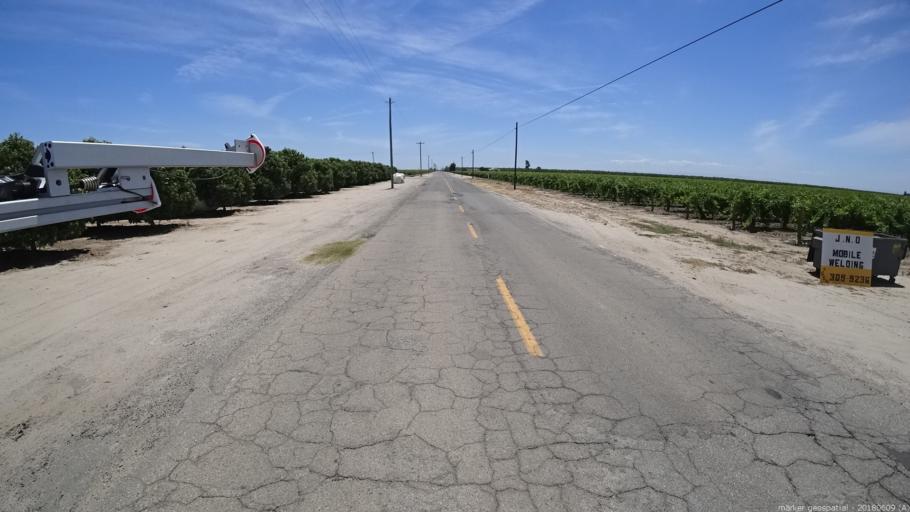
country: US
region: California
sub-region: Madera County
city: Parkwood
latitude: 36.8594
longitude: -120.0922
